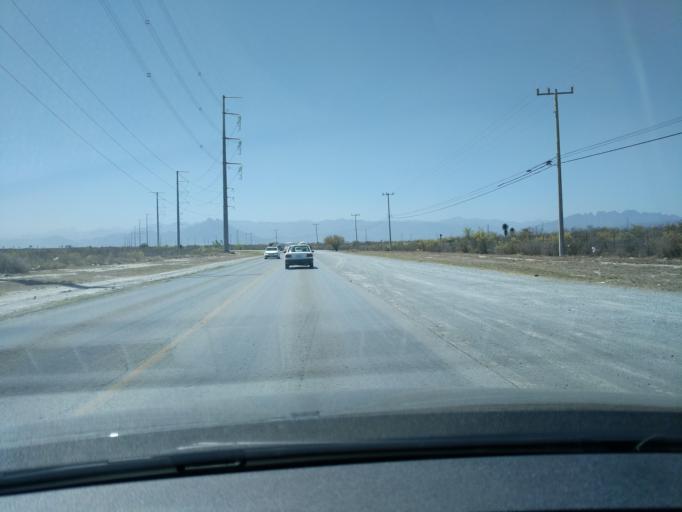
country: MX
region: Nuevo Leon
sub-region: Apodaca
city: Artemio Trevino
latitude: 25.8317
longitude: -100.1414
